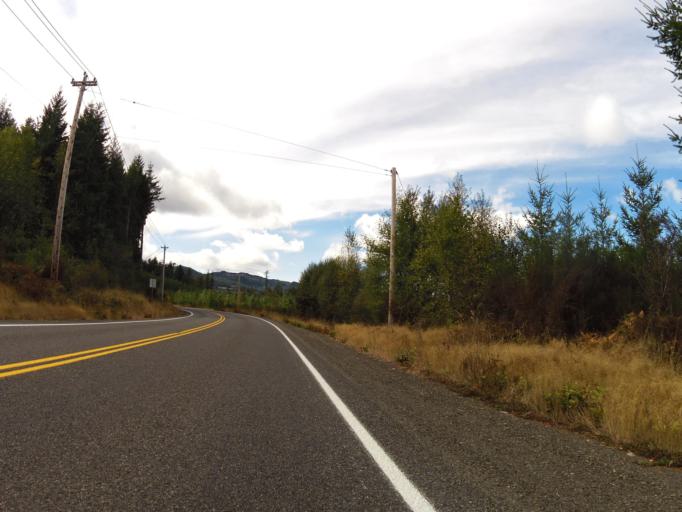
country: US
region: Washington
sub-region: Mason County
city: Shelton
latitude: 47.1477
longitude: -123.0738
